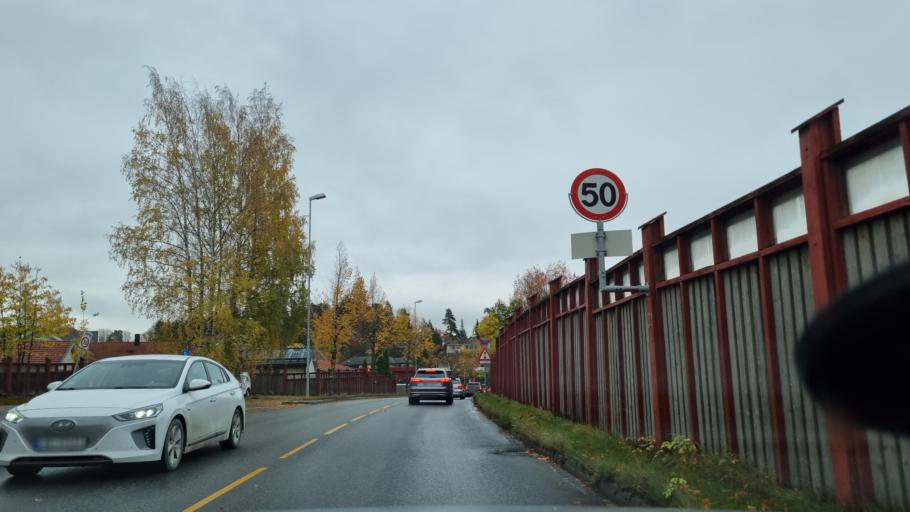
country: NO
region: Hedmark
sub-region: Hamar
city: Hamar
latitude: 60.8056
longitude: 11.0690
